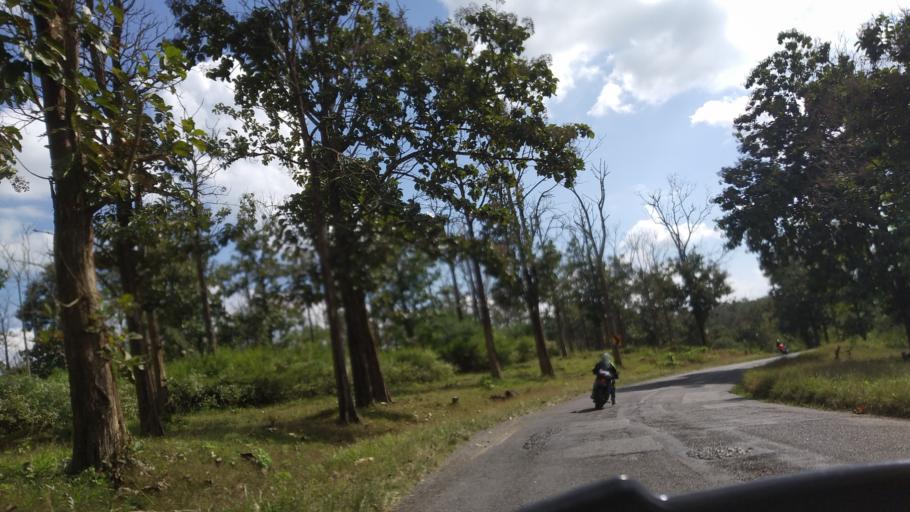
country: IN
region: Kerala
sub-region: Wayanad
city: Panamaram
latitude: 11.9219
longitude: 76.0663
